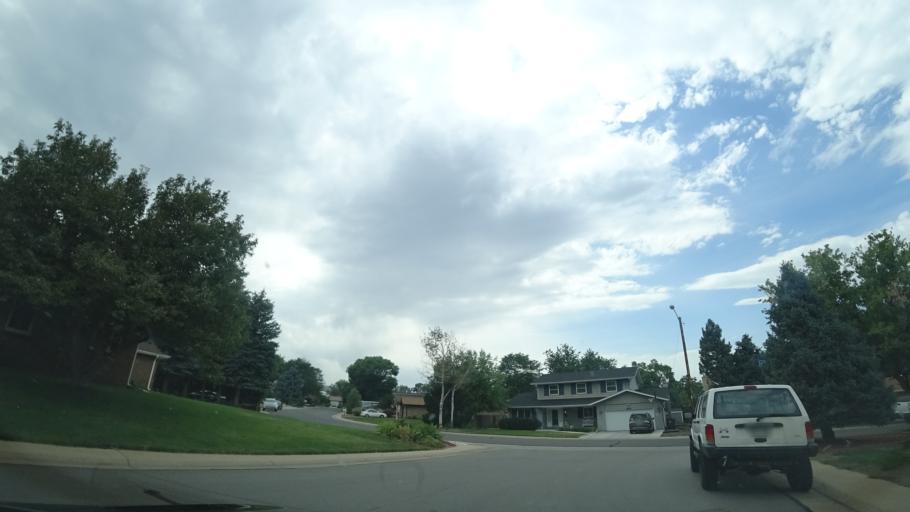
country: US
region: Colorado
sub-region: Jefferson County
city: Lakewood
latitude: 39.7080
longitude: -105.1052
